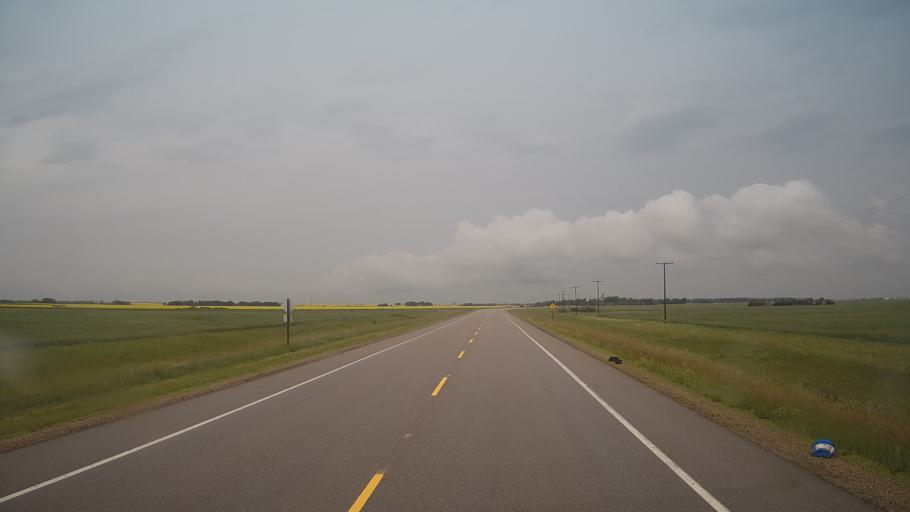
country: CA
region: Saskatchewan
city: Wilkie
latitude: 52.3268
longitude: -108.7087
